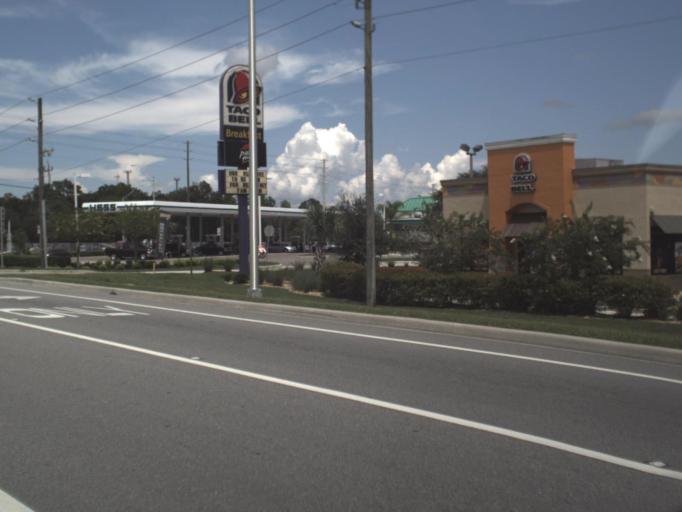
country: US
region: Florida
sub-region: Pasco County
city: Wesley Chapel
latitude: 28.2353
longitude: -82.3499
